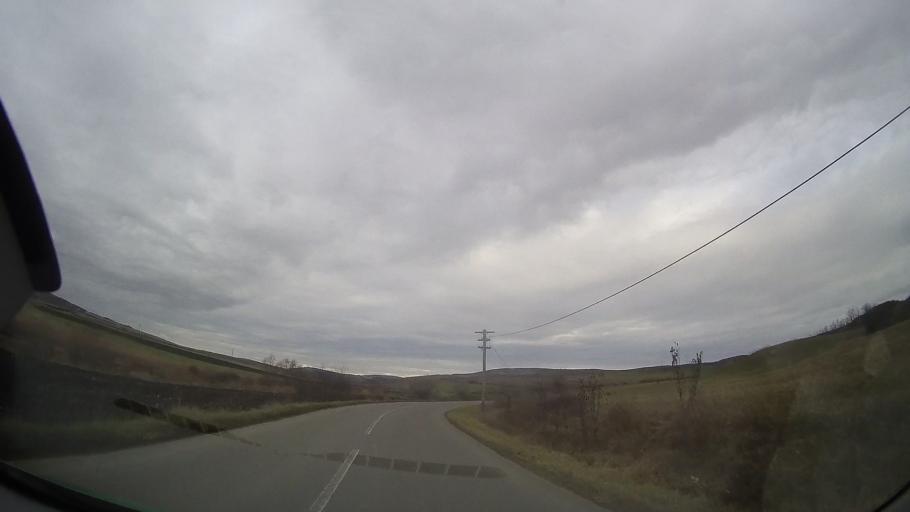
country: RO
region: Mures
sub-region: Comuna Faragau
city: Faragau
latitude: 46.7405
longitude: 24.5380
